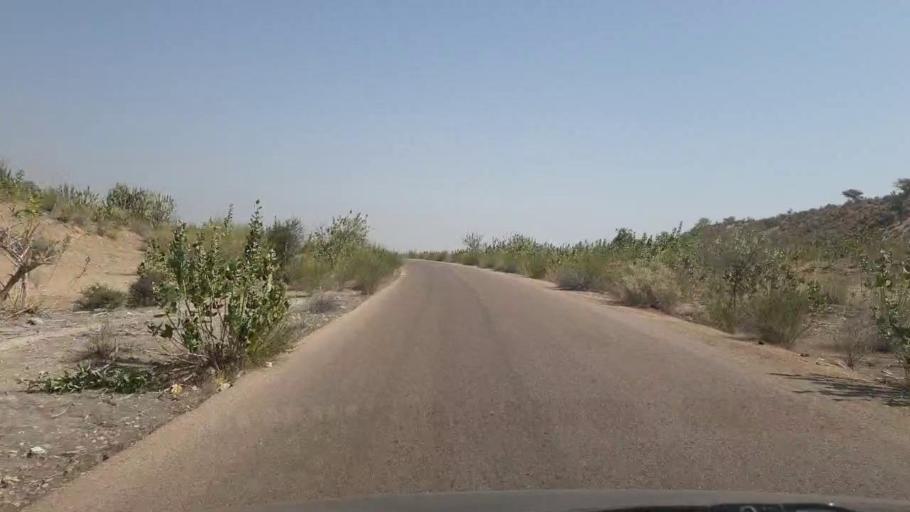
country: PK
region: Sindh
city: Chor
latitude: 25.6131
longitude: 70.0474
